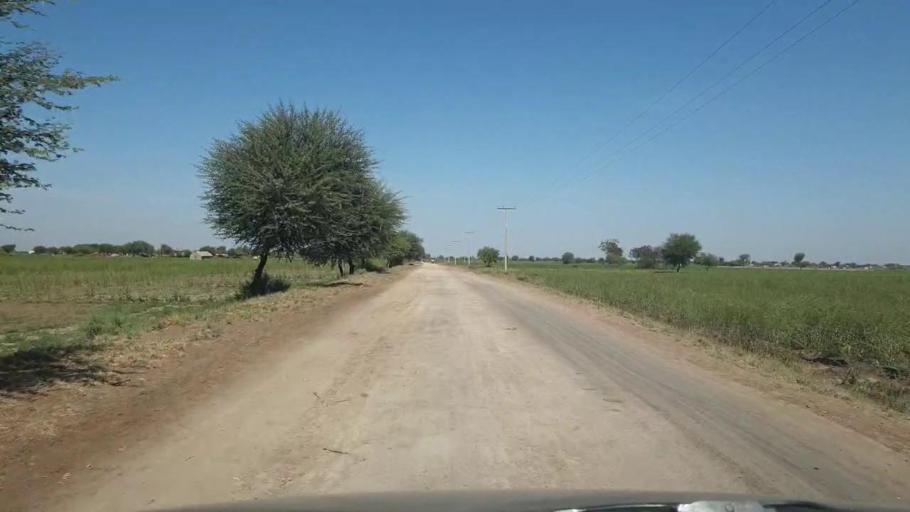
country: PK
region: Sindh
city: Dhoro Naro
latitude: 25.4152
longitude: 69.6178
